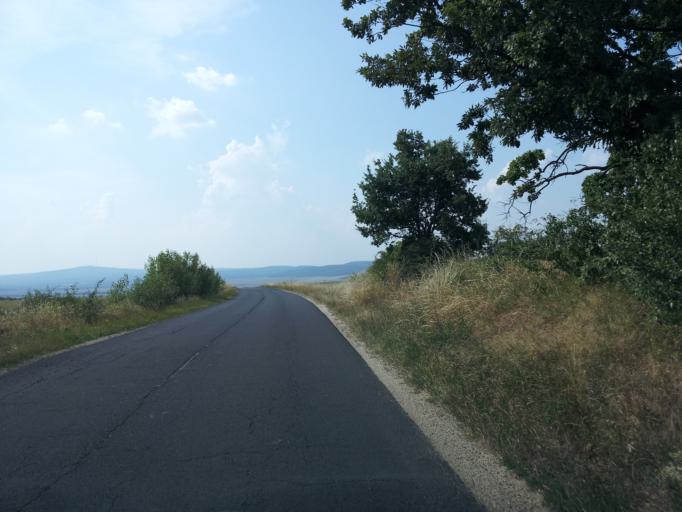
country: HU
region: Veszprem
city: Balatonfured
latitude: 46.9971
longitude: 17.8013
